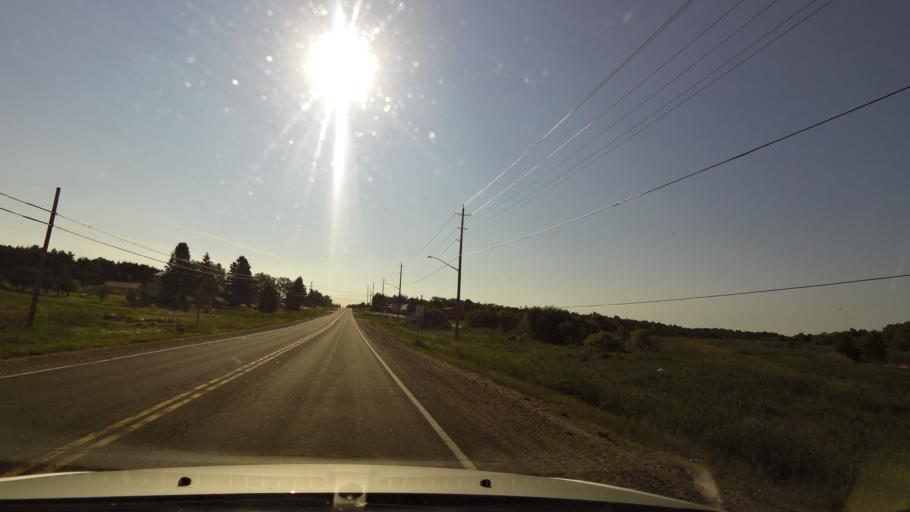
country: CA
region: Ontario
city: Greater Sudbury
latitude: 46.1047
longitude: -80.6137
